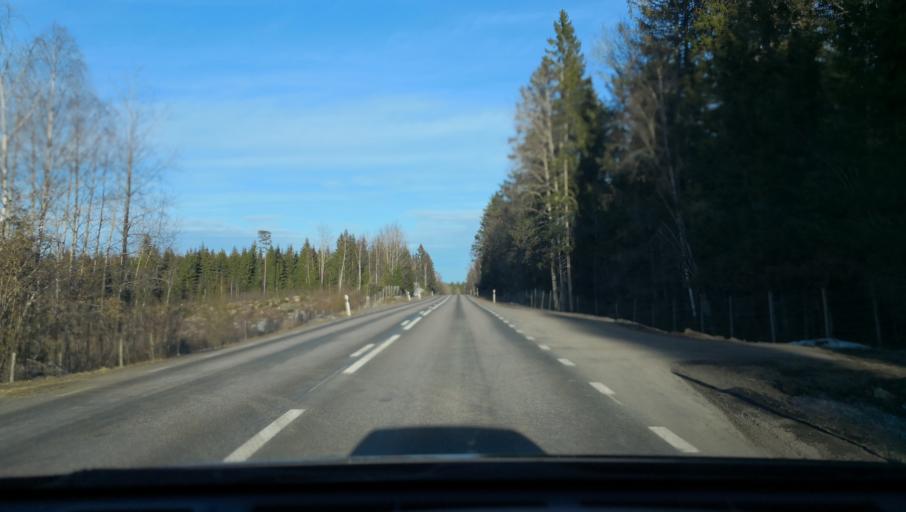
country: SE
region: Uppsala
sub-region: Osthammars Kommun
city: Gimo
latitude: 60.2241
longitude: 18.2412
